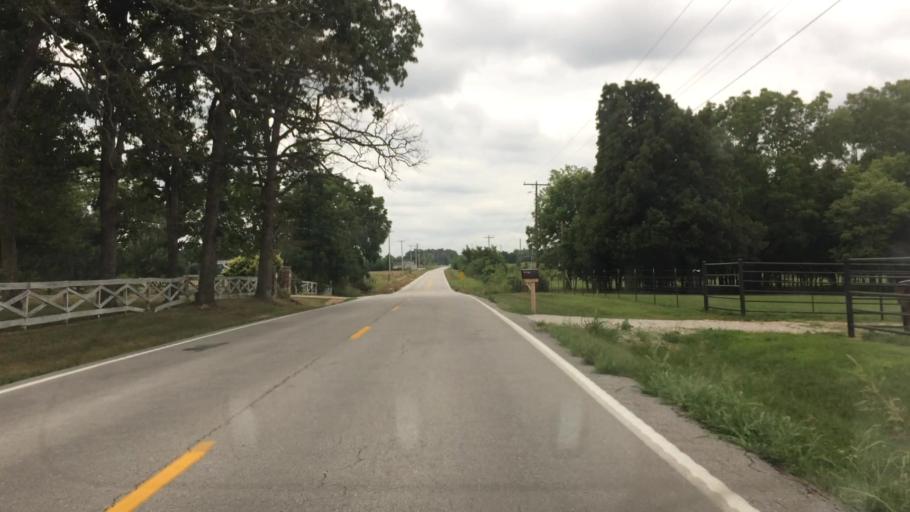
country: US
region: Missouri
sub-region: Greene County
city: Strafford
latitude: 37.2888
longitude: -93.1131
